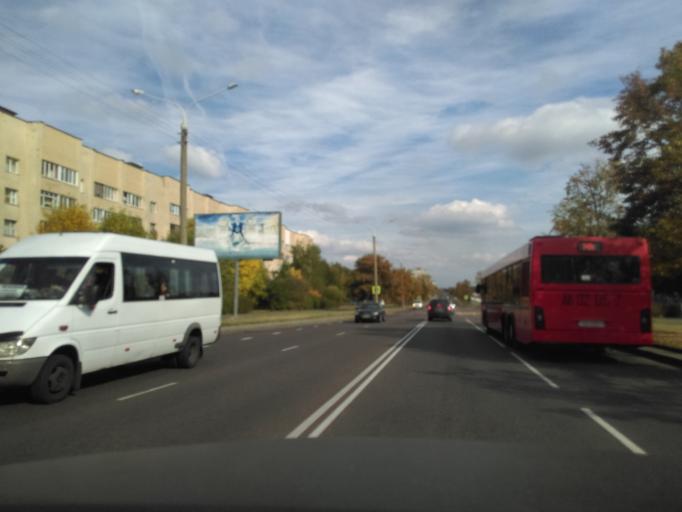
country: BY
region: Minsk
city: Machulishchy
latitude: 53.8342
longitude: 27.6104
